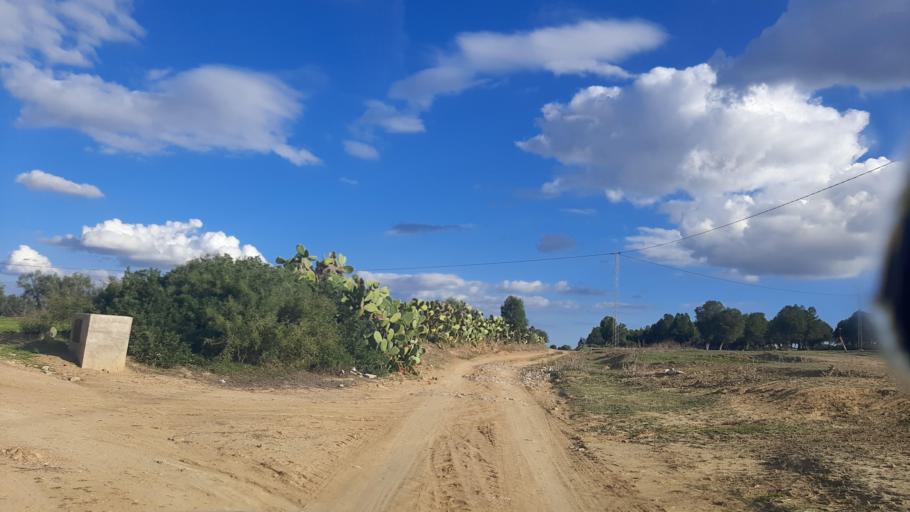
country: TN
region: Nabul
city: Bu `Urqub
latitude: 36.4601
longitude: 10.4895
